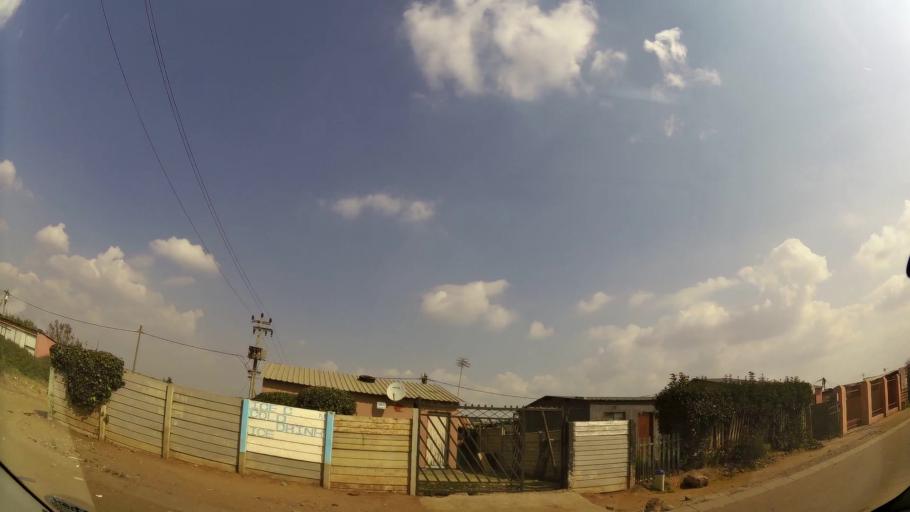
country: ZA
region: Gauteng
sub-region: Ekurhuleni Metropolitan Municipality
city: Springs
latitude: -26.1309
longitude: 28.4812
